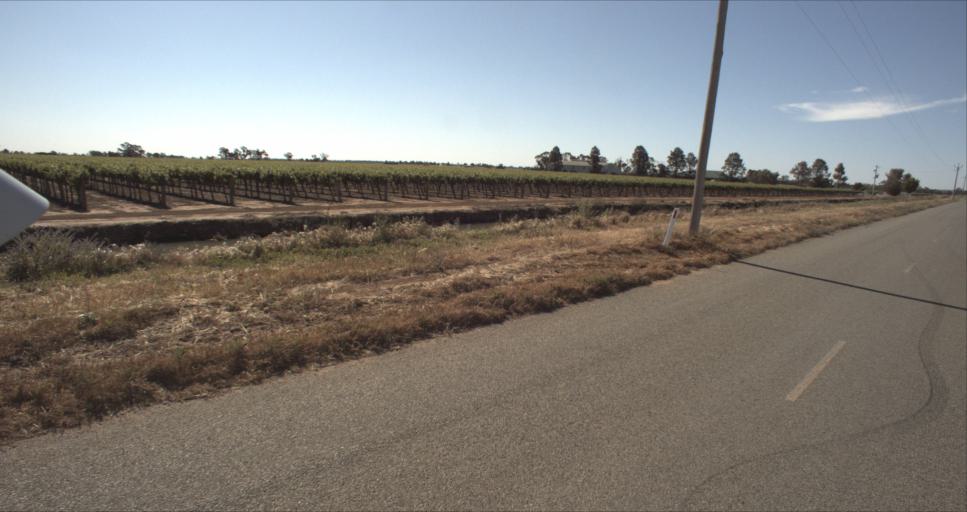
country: AU
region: New South Wales
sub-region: Leeton
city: Leeton
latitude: -34.5834
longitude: 146.3794
